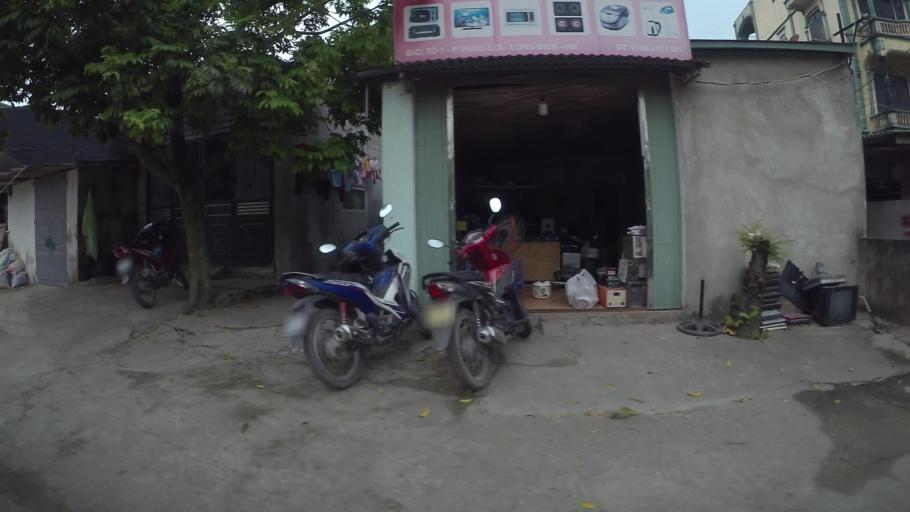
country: VN
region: Ha Noi
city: Trau Quy
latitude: 21.0527
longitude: 105.9232
